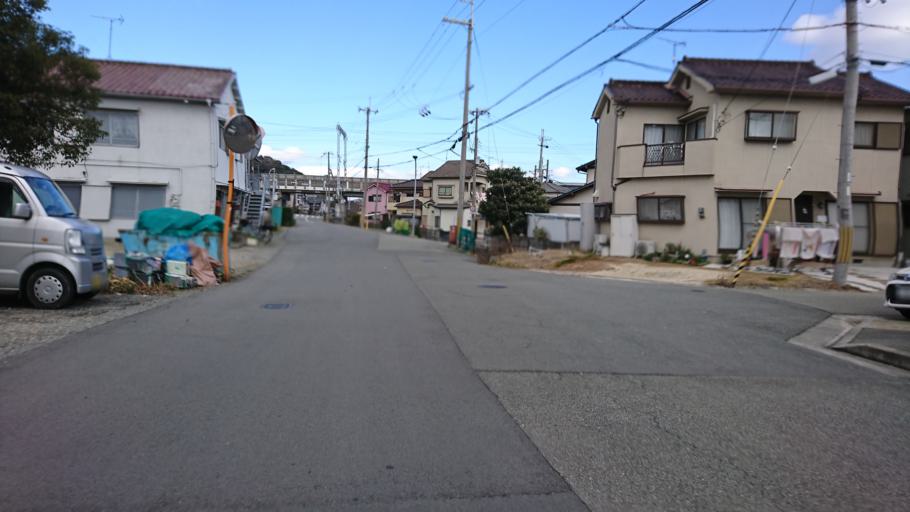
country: JP
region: Hyogo
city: Kakogawacho-honmachi
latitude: 34.7696
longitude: 134.7936
